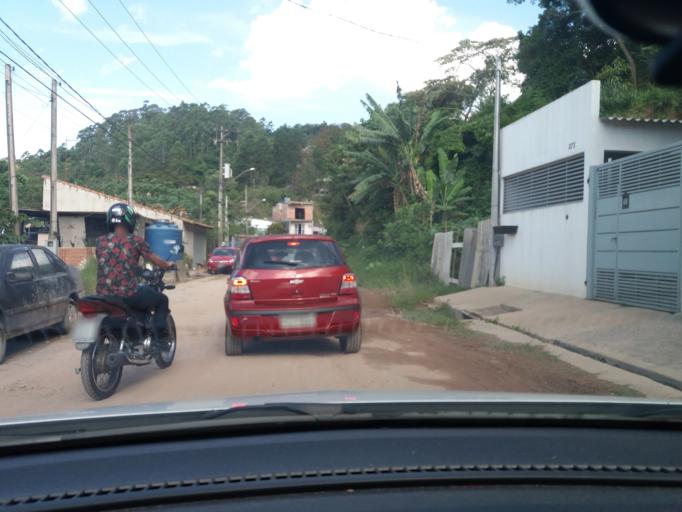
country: BR
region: Sao Paulo
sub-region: Mairipora
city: Mairipora
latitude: -23.3742
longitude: -46.5736
